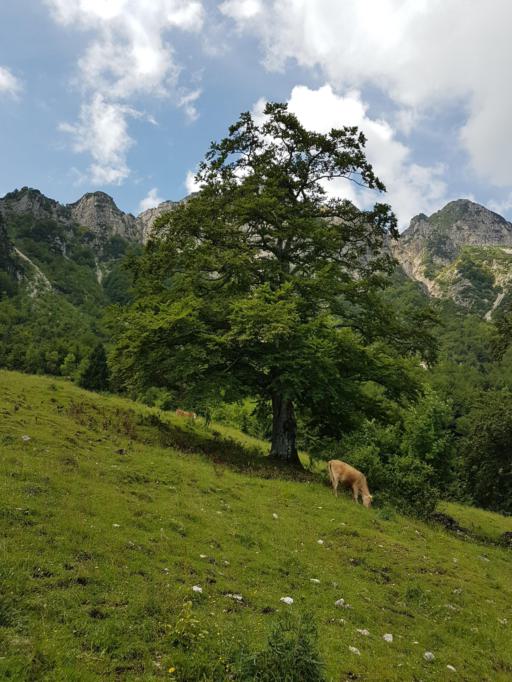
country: IT
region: Veneto
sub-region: Provincia di Vicenza
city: Recoaro Terme
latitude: 45.6827
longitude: 11.1784
